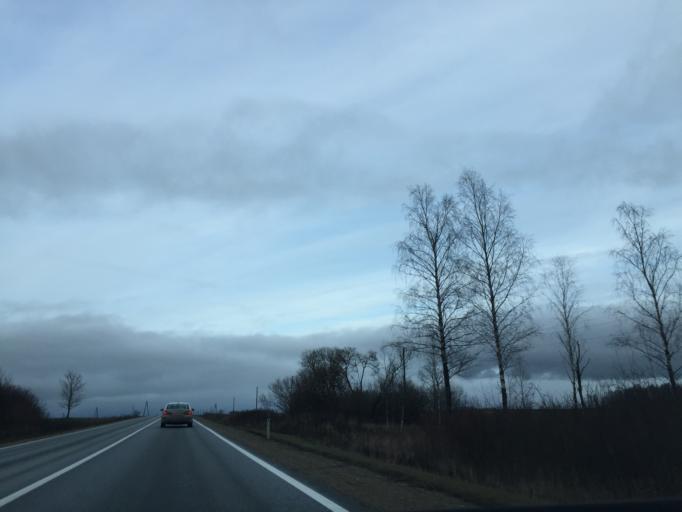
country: LV
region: Dobeles Rajons
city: Dobele
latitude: 56.7223
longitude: 23.1991
